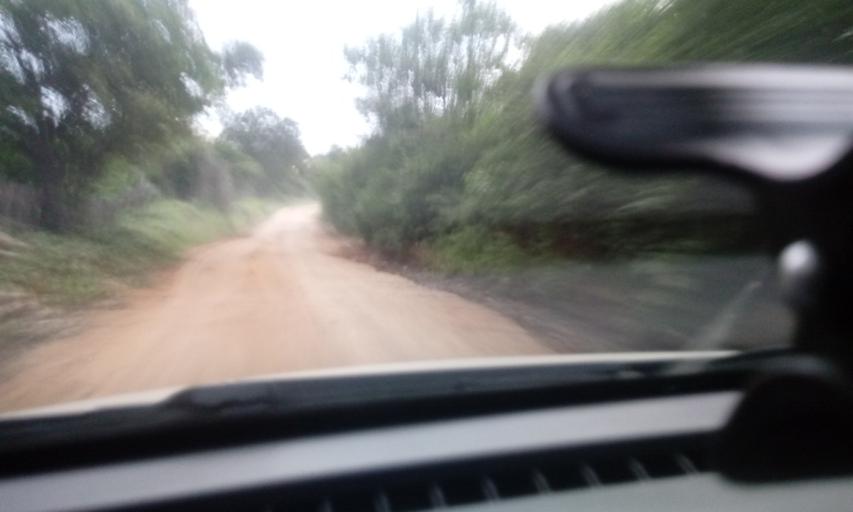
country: BR
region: Bahia
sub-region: Riacho De Santana
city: Riacho de Santana
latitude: -13.8057
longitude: -42.7557
